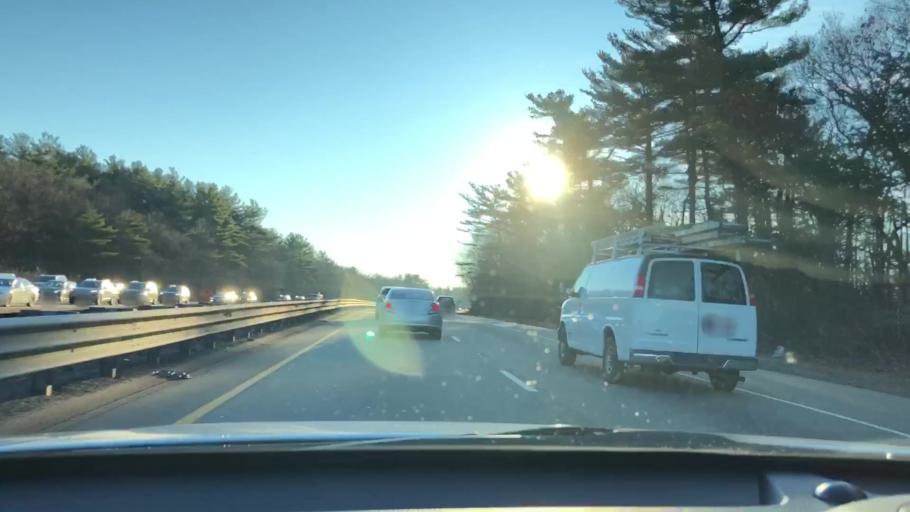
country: US
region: Massachusetts
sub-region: Norfolk County
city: Weymouth
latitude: 42.1834
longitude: -70.9233
